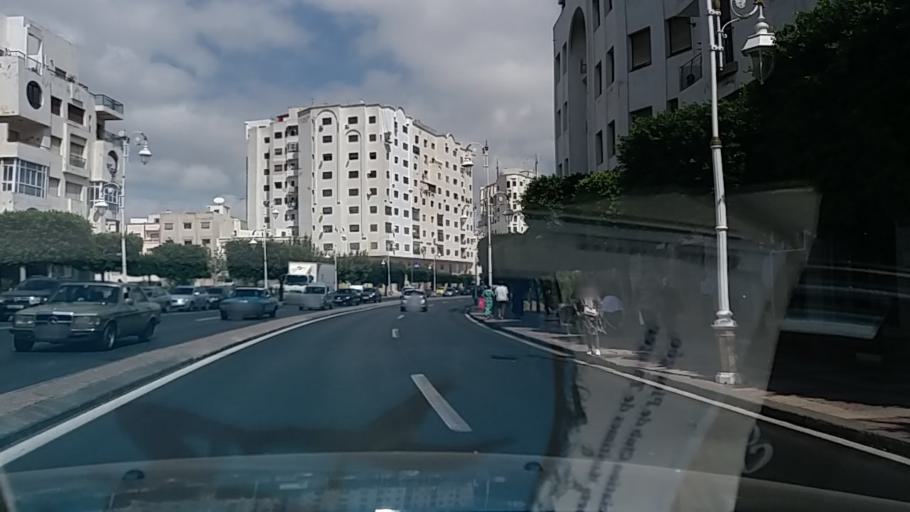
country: MA
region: Tanger-Tetouan
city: Tetouan
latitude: 35.5741
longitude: -5.3601
